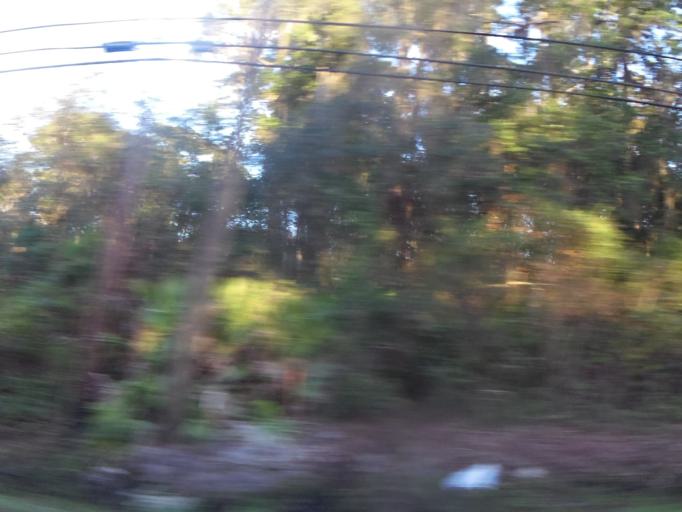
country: US
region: Florida
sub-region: Putnam County
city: East Palatka
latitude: 29.8324
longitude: -81.5535
